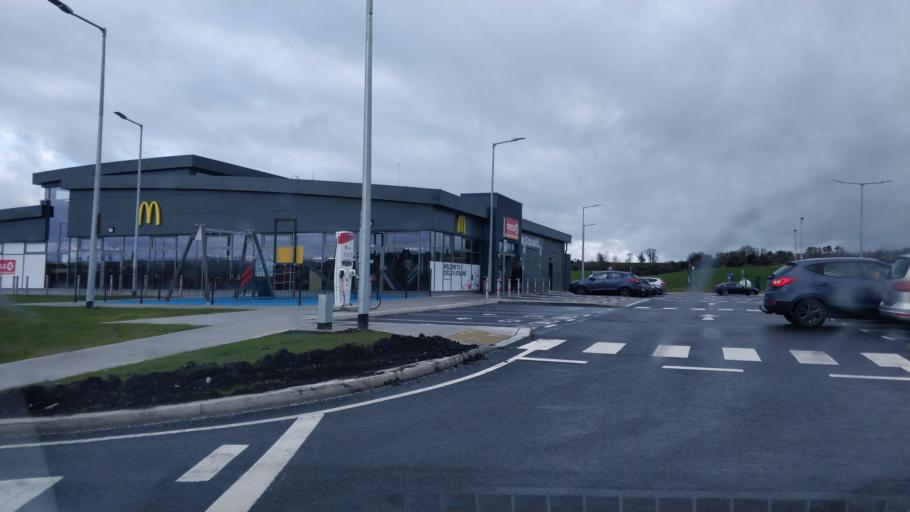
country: IE
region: Leinster
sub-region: An Iarmhi
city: Moate
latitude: 53.4003
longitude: -7.8270
